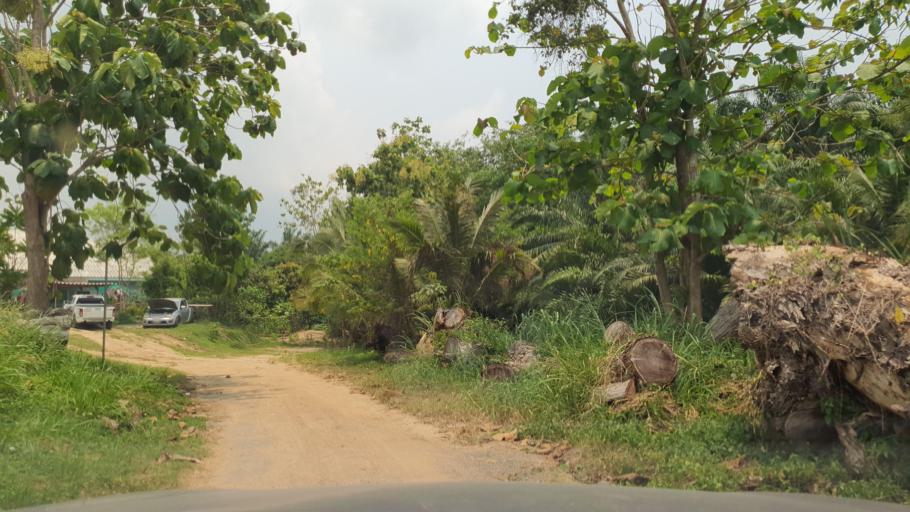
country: TH
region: Rayong
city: Ban Chang
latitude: 12.7669
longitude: 100.9896
